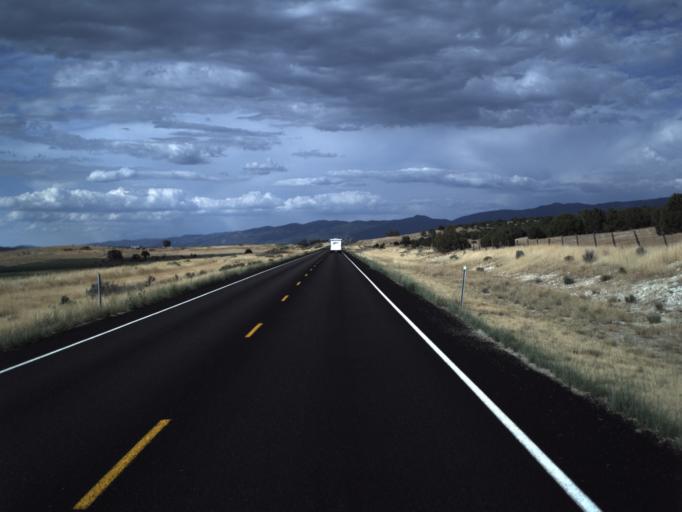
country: US
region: Utah
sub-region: Sanpete County
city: Moroni
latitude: 39.4701
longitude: -111.5306
